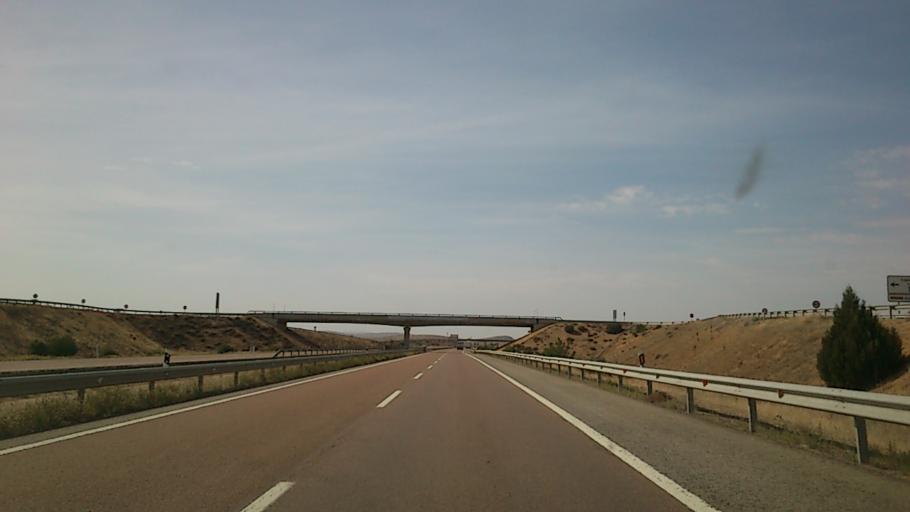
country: ES
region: Aragon
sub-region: Provincia de Teruel
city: Singra
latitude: 40.6203
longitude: -1.2957
